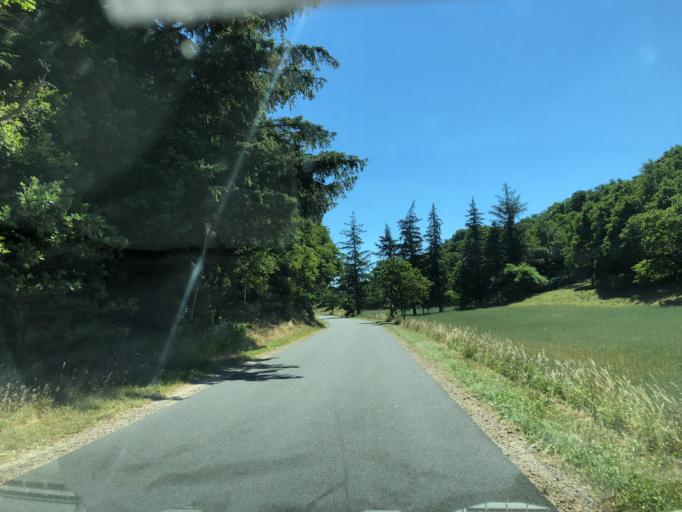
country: DK
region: Central Jutland
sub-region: Viborg Kommune
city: Viborg
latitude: 56.5426
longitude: 9.4576
